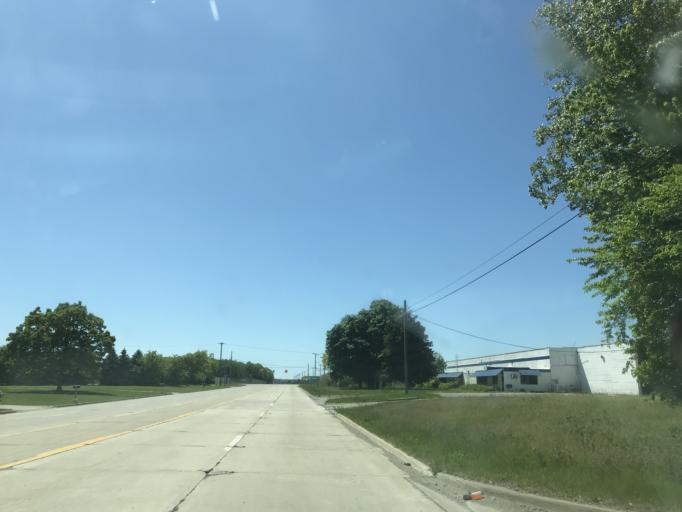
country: US
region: Michigan
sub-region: Wayne County
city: Taylor
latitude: 42.2101
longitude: -83.3236
